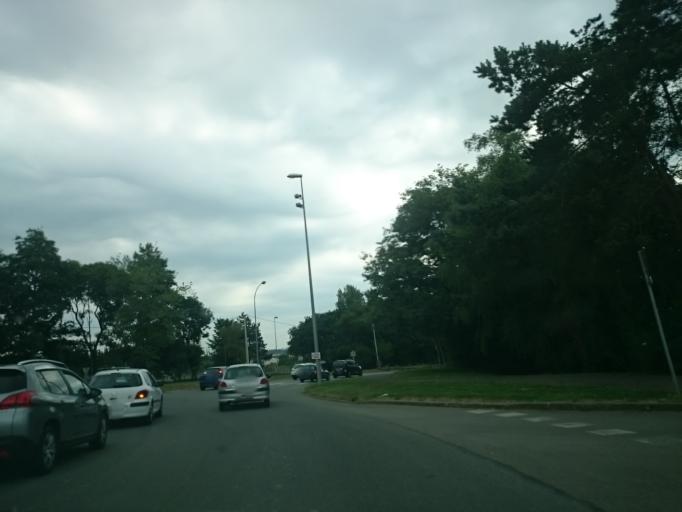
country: FR
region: Brittany
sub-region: Departement du Finistere
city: Bohars
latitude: 48.4131
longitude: -4.5085
